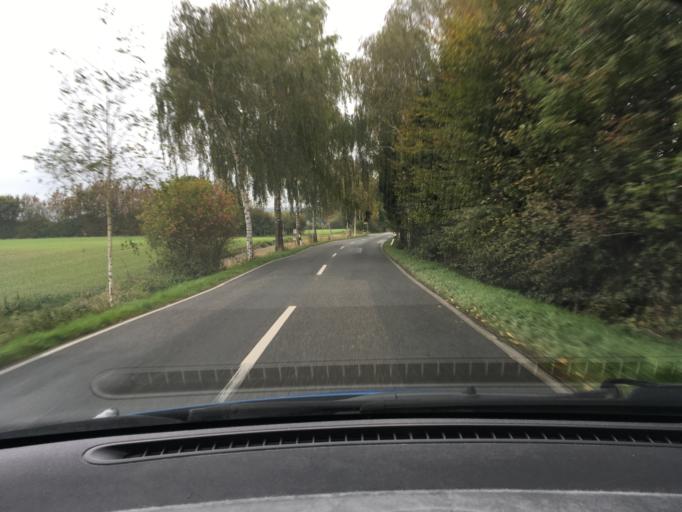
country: DE
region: Schleswig-Holstein
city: Bosau
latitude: 54.1013
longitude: 10.4414
